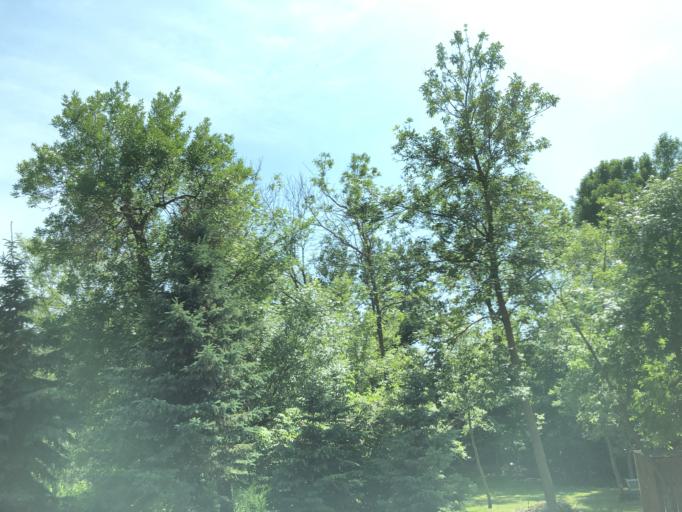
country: US
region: Minnesota
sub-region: Douglas County
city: Alexandria
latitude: 45.9307
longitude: -95.3766
